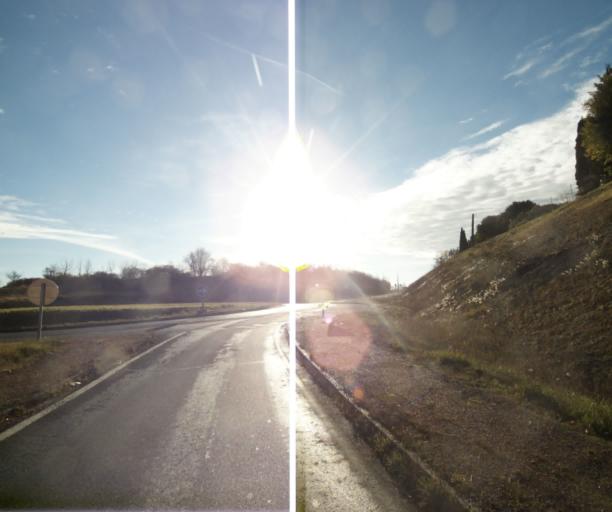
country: FR
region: Poitou-Charentes
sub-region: Departement de la Charente-Maritime
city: Saintes
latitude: 45.7446
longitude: -0.6755
